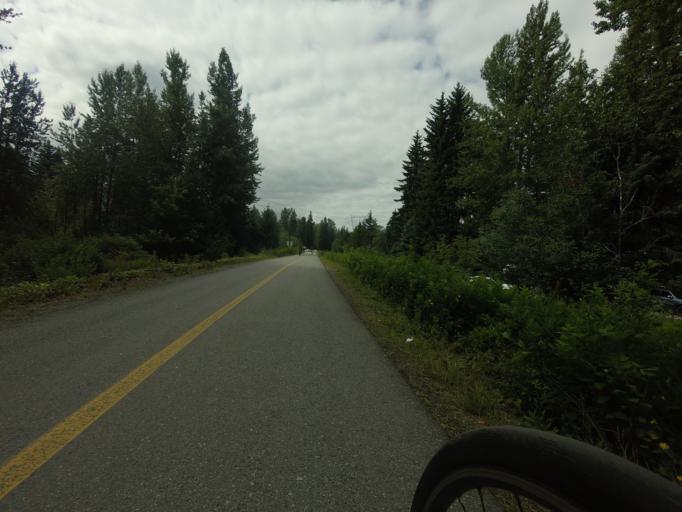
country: CA
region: British Columbia
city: Whistler
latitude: 50.1379
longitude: -122.9500
